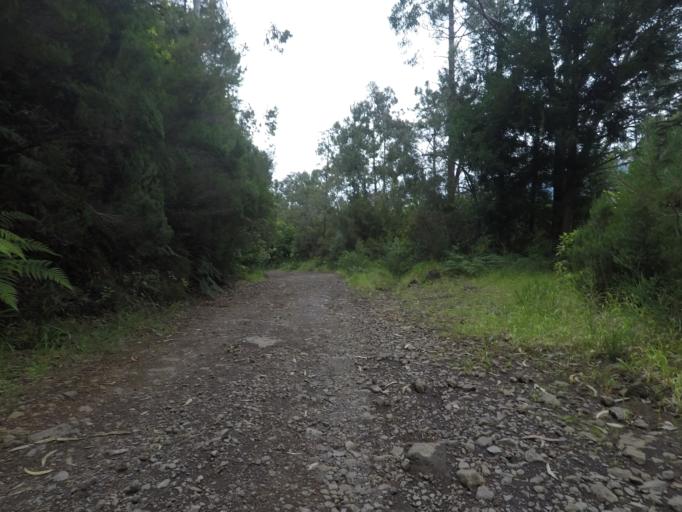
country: PT
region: Madeira
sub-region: Sao Vicente
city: Sao Vicente
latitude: 32.7755
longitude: -17.0478
